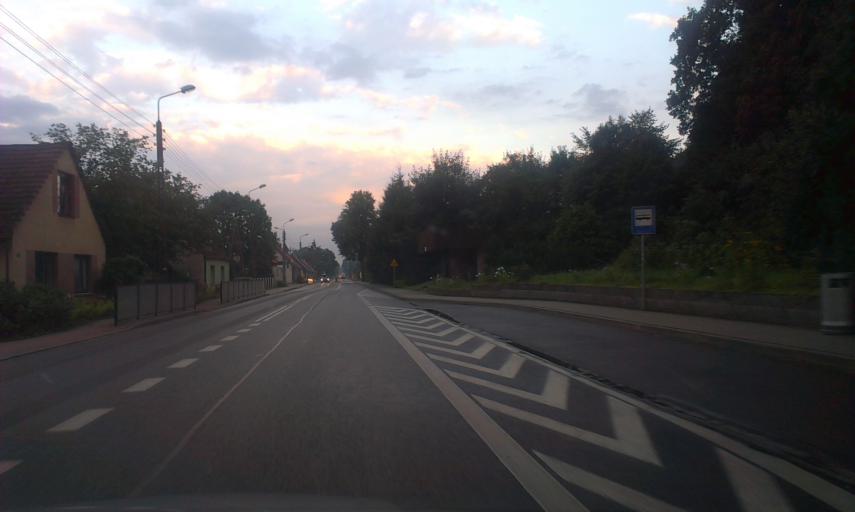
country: PL
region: West Pomeranian Voivodeship
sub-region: Powiat koszalinski
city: Sianow
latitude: 54.1270
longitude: 16.2985
